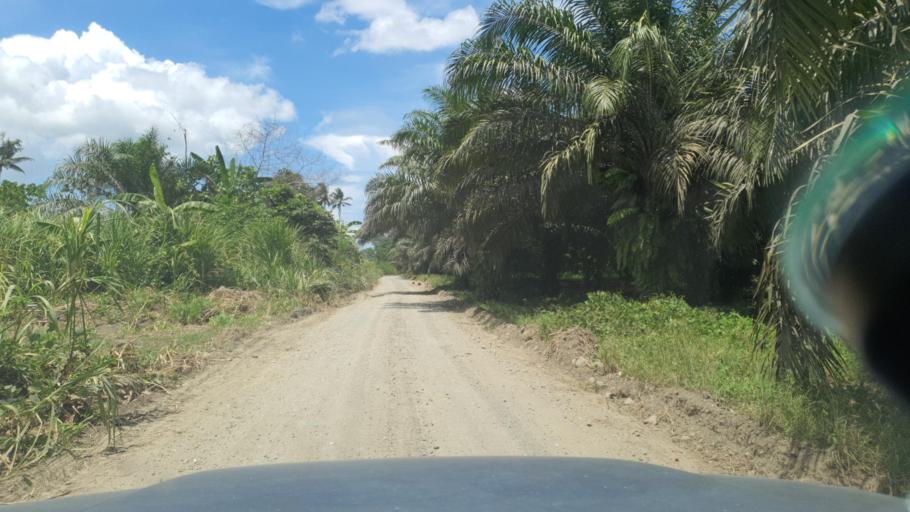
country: SB
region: Guadalcanal
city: Honiara
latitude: -9.4810
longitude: 160.1364
